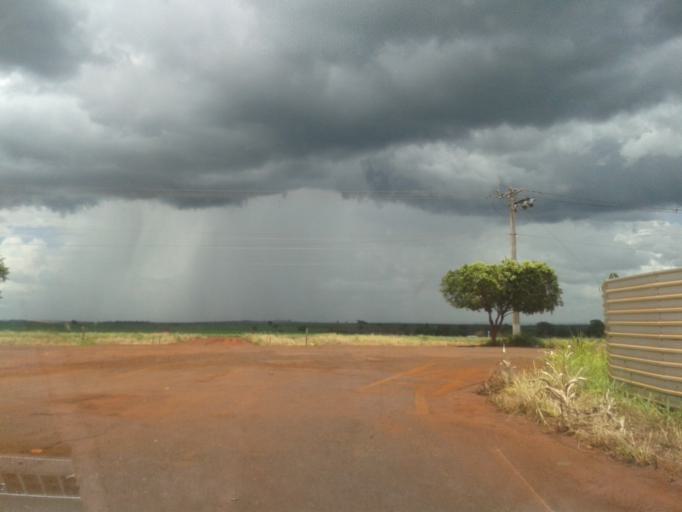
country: BR
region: Minas Gerais
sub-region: Centralina
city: Centralina
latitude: -18.6014
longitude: -49.1945
